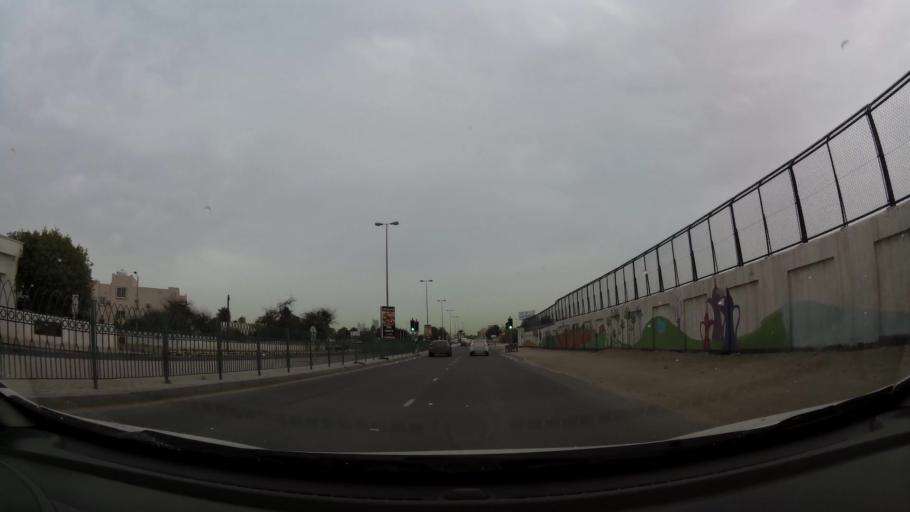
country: BH
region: Manama
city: Jidd Hafs
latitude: 26.2186
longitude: 50.5275
